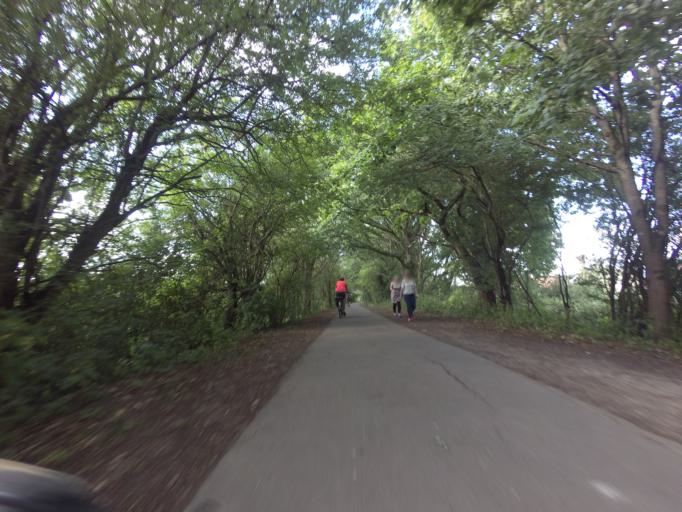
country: GB
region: England
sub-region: East Sussex
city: Hailsham
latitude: 50.8798
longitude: 0.2496
